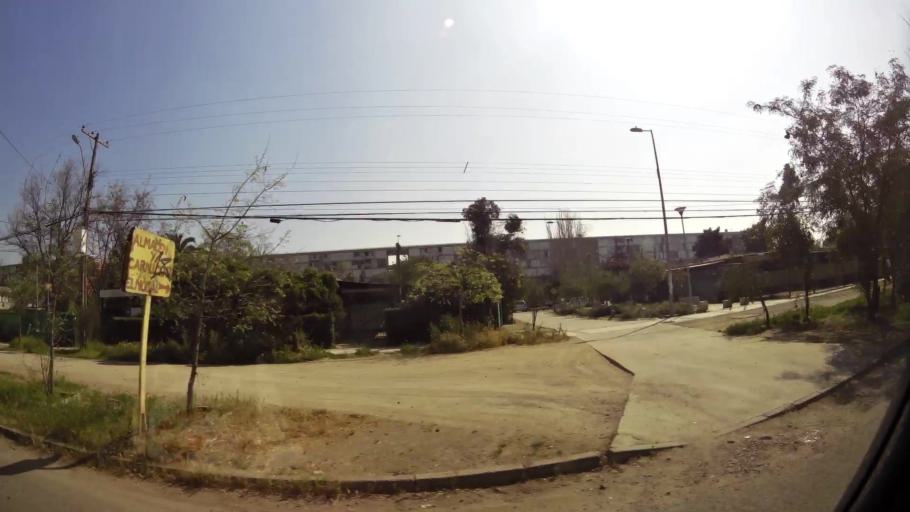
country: CL
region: Santiago Metropolitan
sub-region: Provincia de Santiago
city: Lo Prado
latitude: -33.4461
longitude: -70.6901
